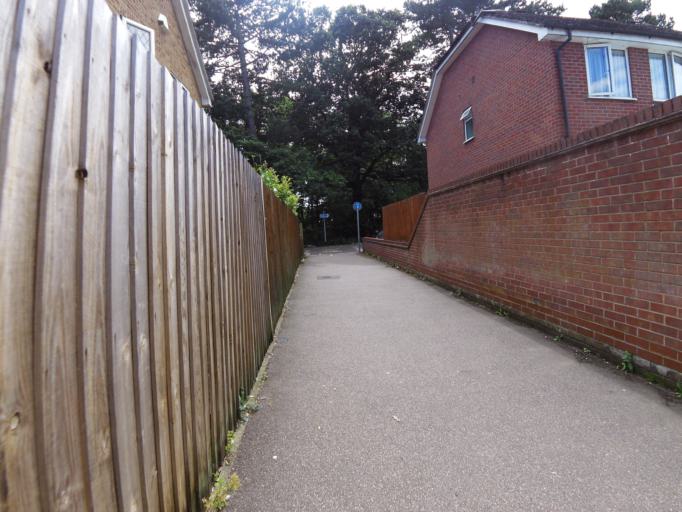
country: GB
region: England
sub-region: Essex
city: Colchester
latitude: 51.9119
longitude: 0.9196
